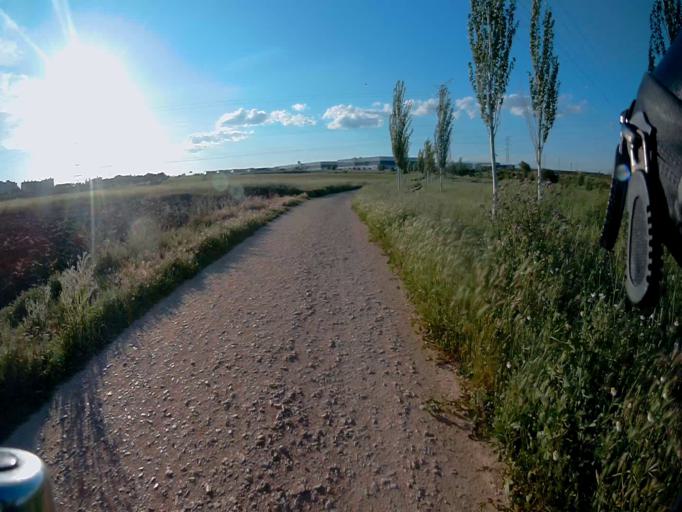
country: ES
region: Madrid
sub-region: Provincia de Madrid
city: Fuenlabrada
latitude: 40.3006
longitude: -3.7980
